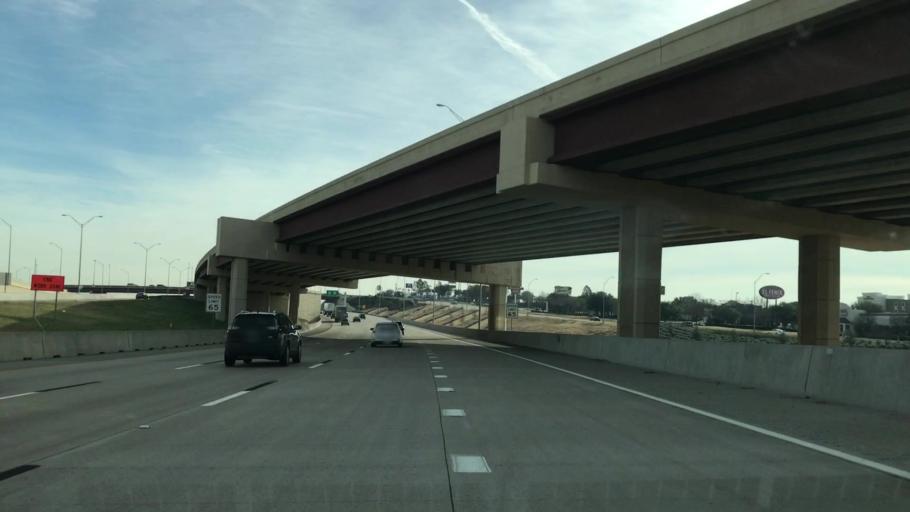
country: US
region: Texas
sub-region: Tarrant County
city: Grapevine
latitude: 32.9230
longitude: -97.0833
